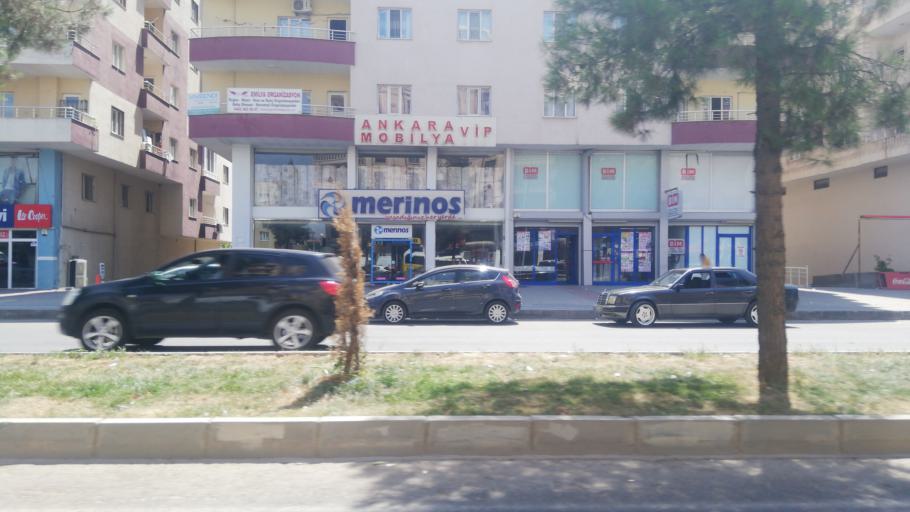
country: TR
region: Mardin
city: Midyat
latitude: 37.4166
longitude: 41.3650
